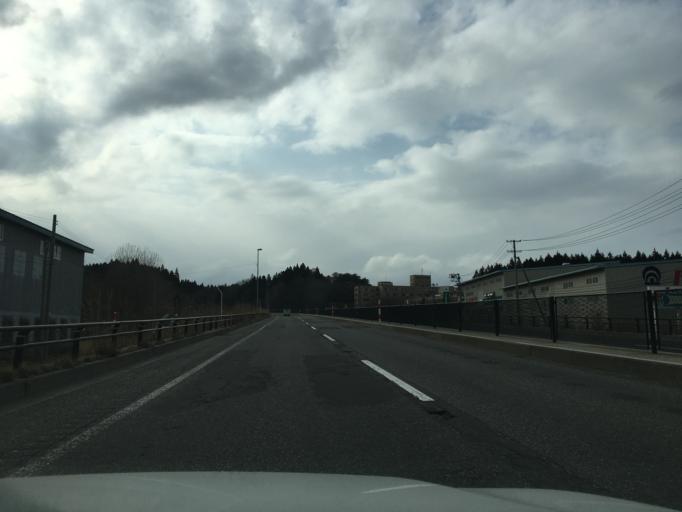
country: JP
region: Aomori
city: Aomori Shi
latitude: 40.8346
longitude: 140.6811
